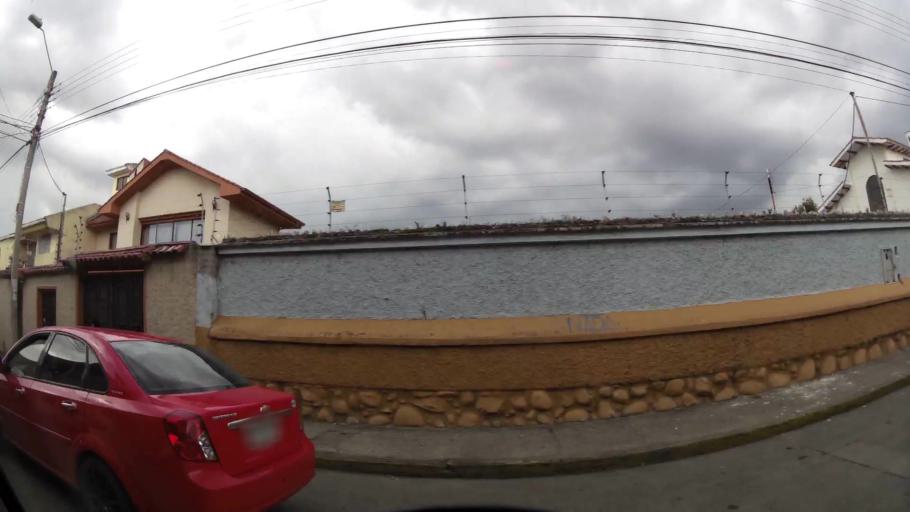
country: EC
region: Azuay
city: Cuenca
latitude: -2.8956
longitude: -79.0124
